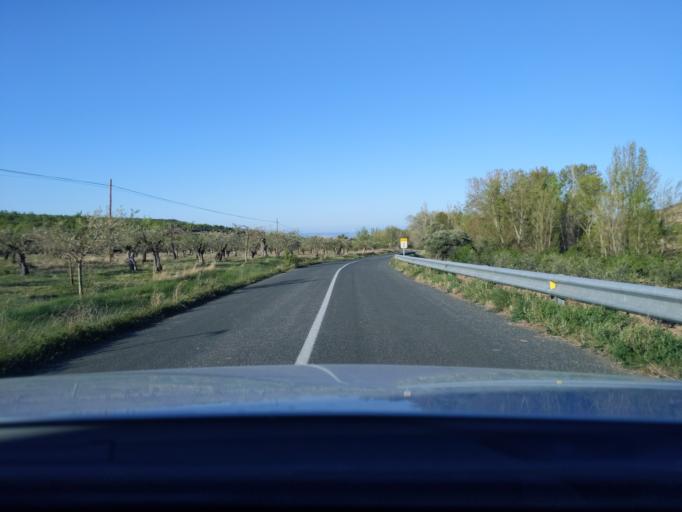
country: ES
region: La Rioja
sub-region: Provincia de La Rioja
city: Bergasa
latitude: 42.2576
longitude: -2.1141
